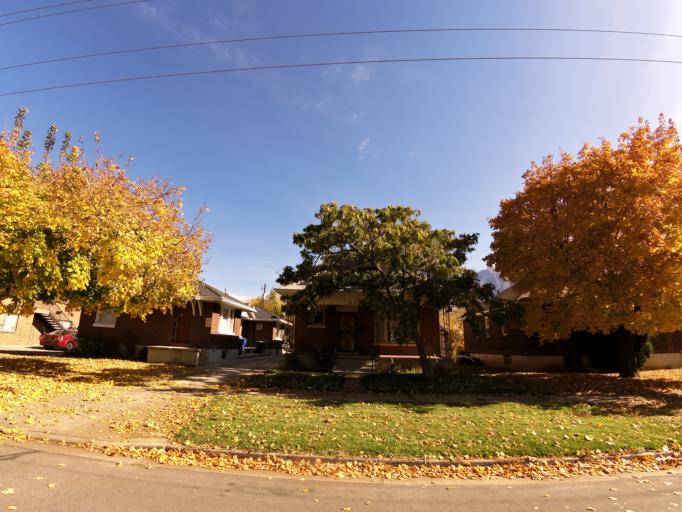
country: US
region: Utah
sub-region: Weber County
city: Ogden
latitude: 41.2282
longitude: -111.9591
